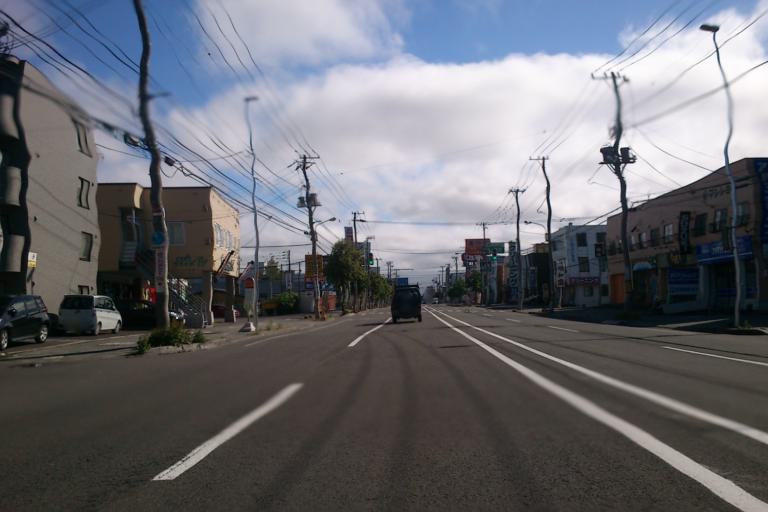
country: JP
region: Hokkaido
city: Sapporo
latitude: 43.1242
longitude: 141.2518
